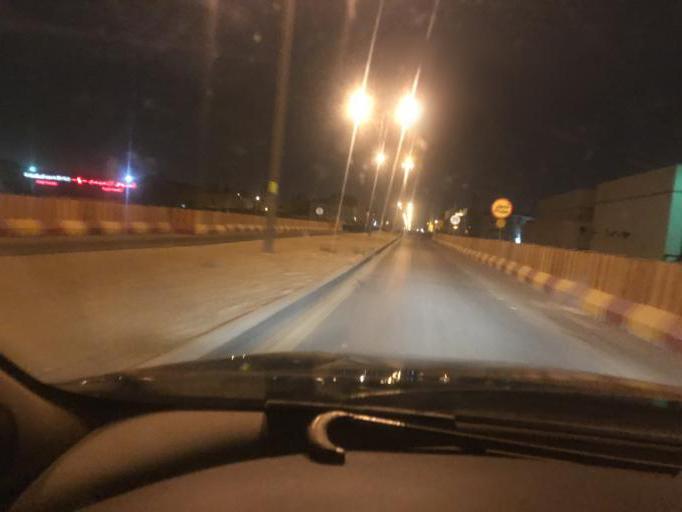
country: SA
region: Ar Riyad
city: Riyadh
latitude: 24.8036
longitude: 46.6752
